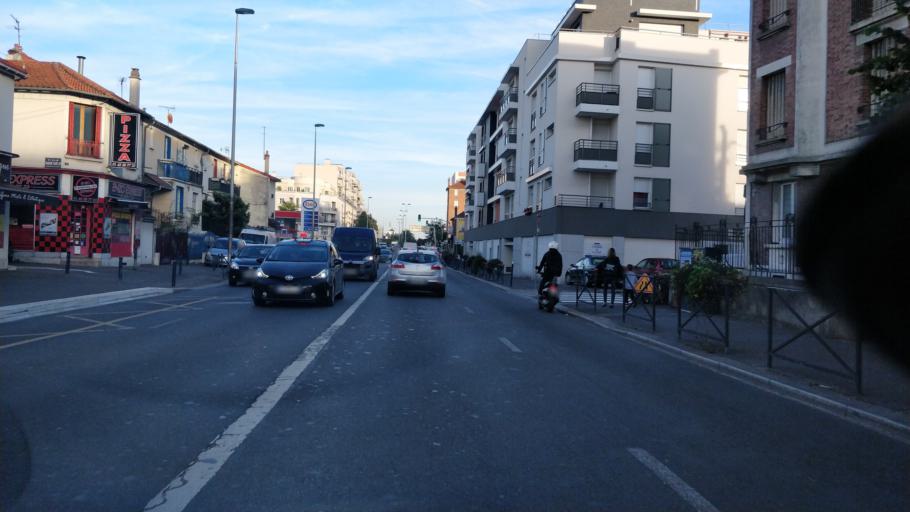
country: FR
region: Ile-de-France
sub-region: Departement de Seine-Saint-Denis
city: Villemomble
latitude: 48.8850
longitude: 2.5054
